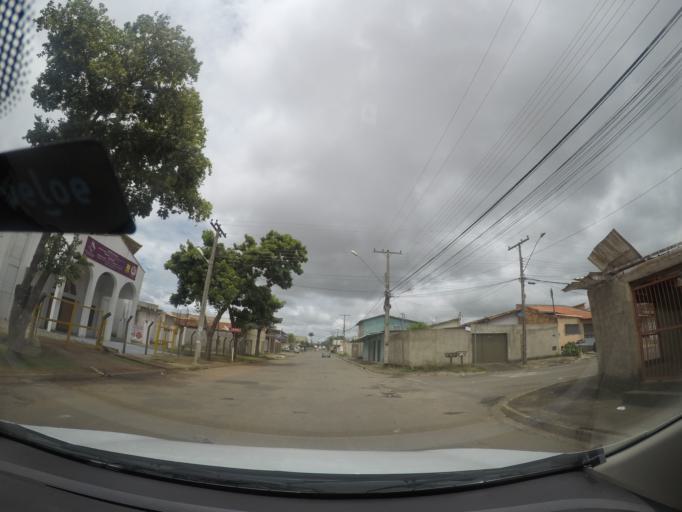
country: BR
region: Goias
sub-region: Goiania
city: Goiania
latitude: -16.7244
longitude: -49.3652
